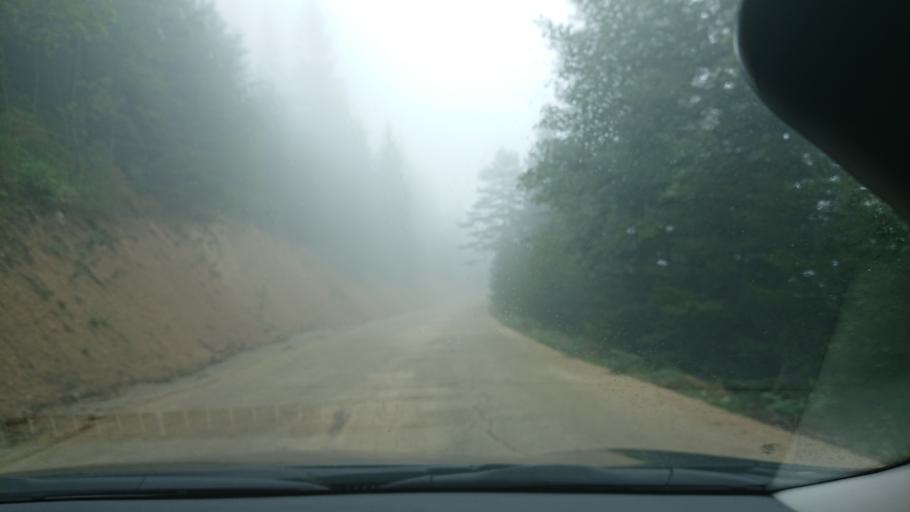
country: TR
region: Gumushane
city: Kurtun
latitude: 40.6629
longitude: 39.0162
